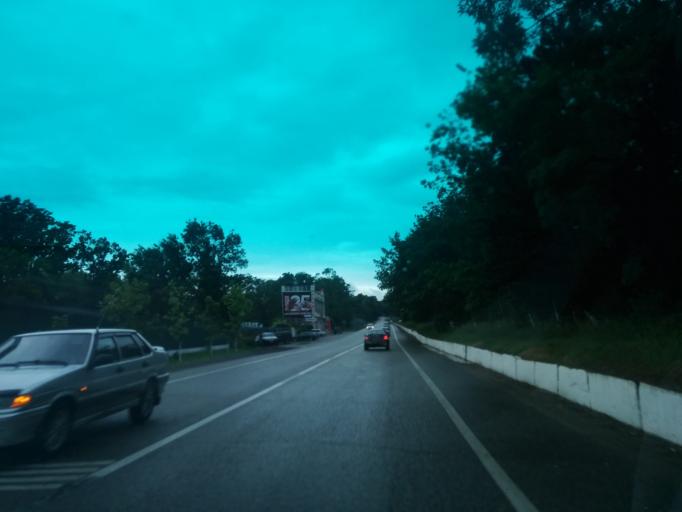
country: RU
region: Krasnodarskiy
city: Agoy
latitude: 44.1423
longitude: 39.0224
